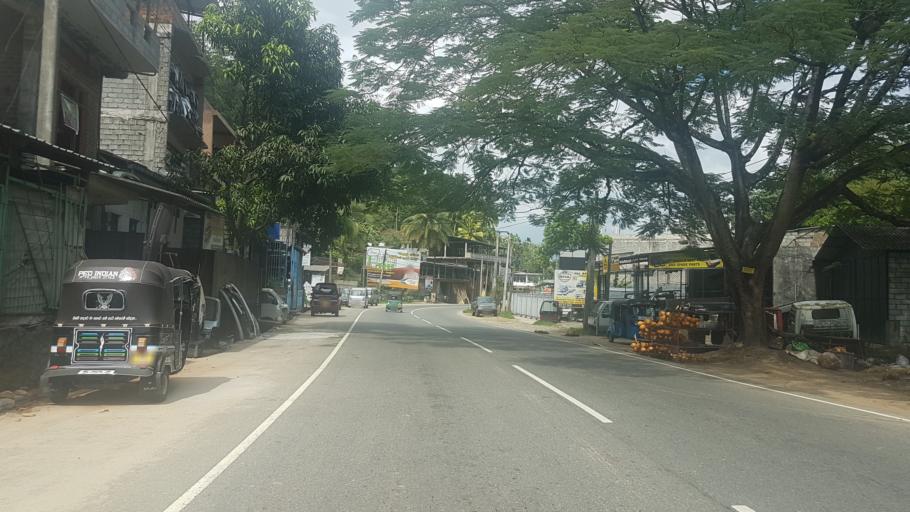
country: LK
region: Central
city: Gampola
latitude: 7.2102
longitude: 80.5986
